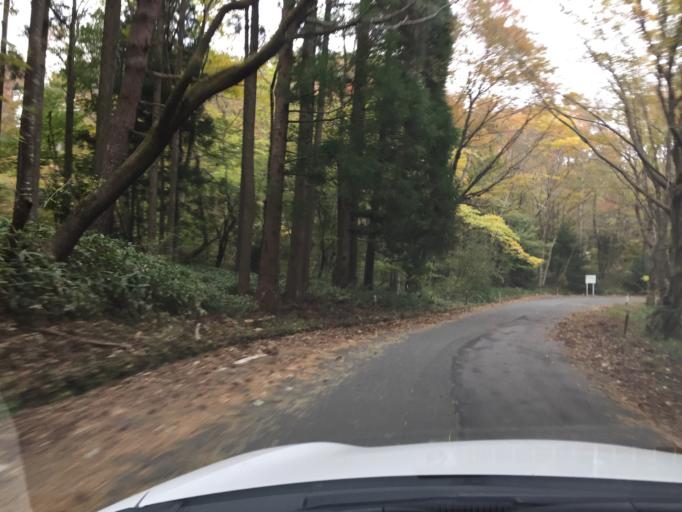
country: JP
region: Fukushima
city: Iwaki
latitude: 37.0993
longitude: 140.8013
